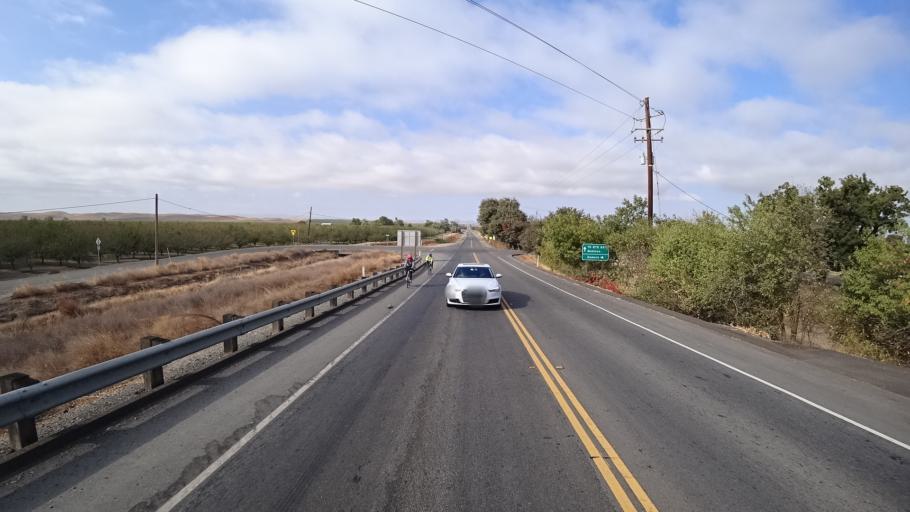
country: US
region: California
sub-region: Yolo County
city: Dunnigan
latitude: 38.7942
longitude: -121.8813
